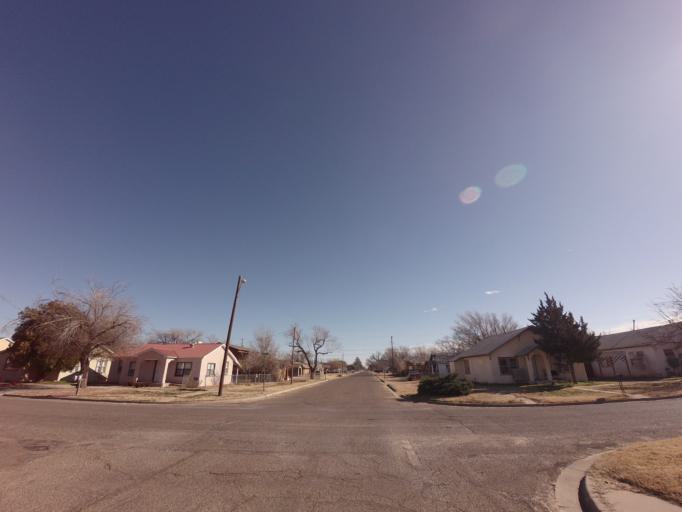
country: US
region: New Mexico
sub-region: Curry County
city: Clovis
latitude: 34.4099
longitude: -103.2119
